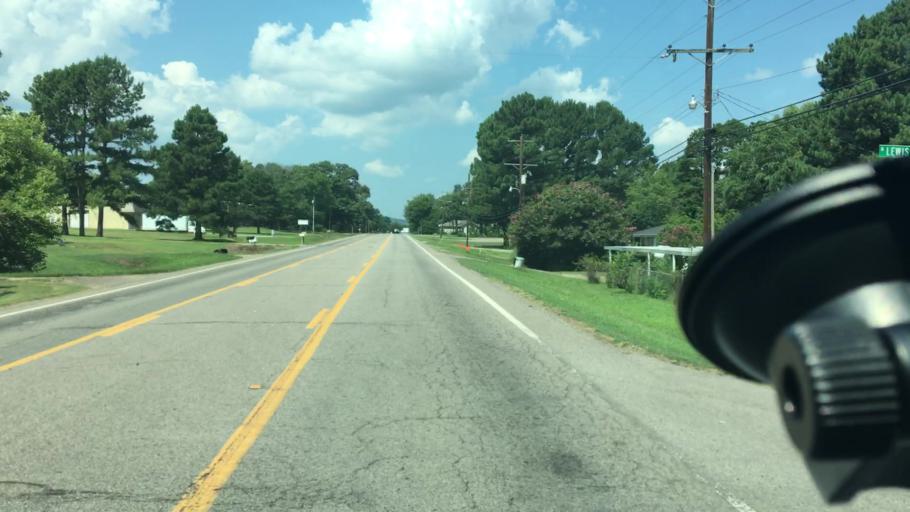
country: US
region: Arkansas
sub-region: Logan County
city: Paris
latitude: 35.2932
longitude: -93.7001
